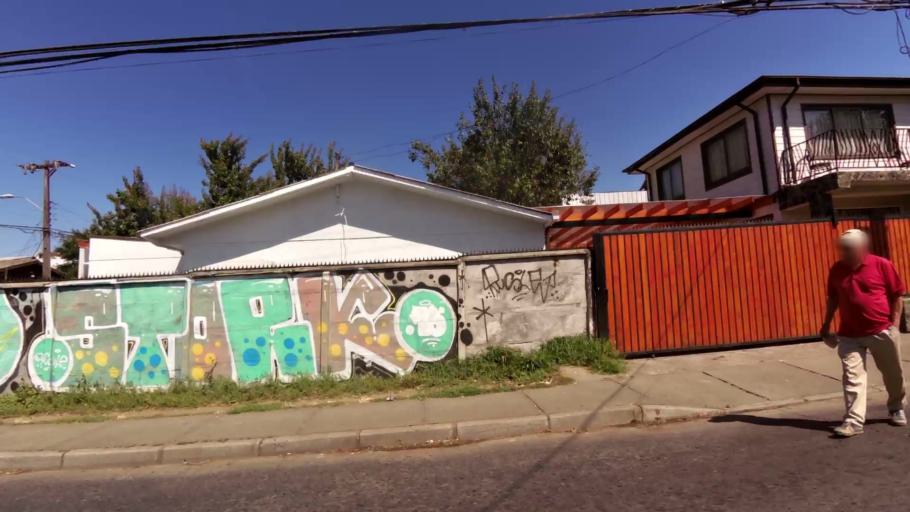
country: CL
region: Biobio
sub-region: Provincia de Concepcion
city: Concepcion
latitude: -36.8015
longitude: -73.0372
